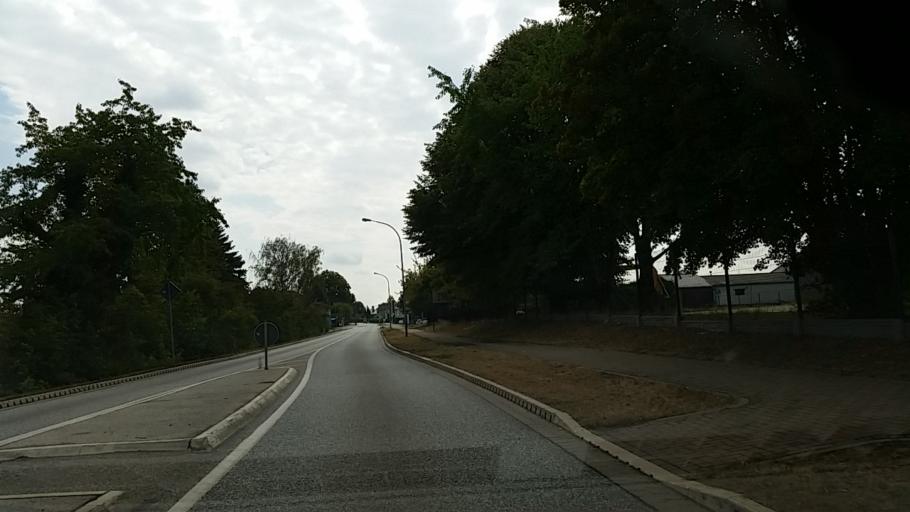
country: DE
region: Saxony-Anhalt
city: Nemsdorf-Gohrendorf
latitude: 51.3462
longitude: 11.6384
